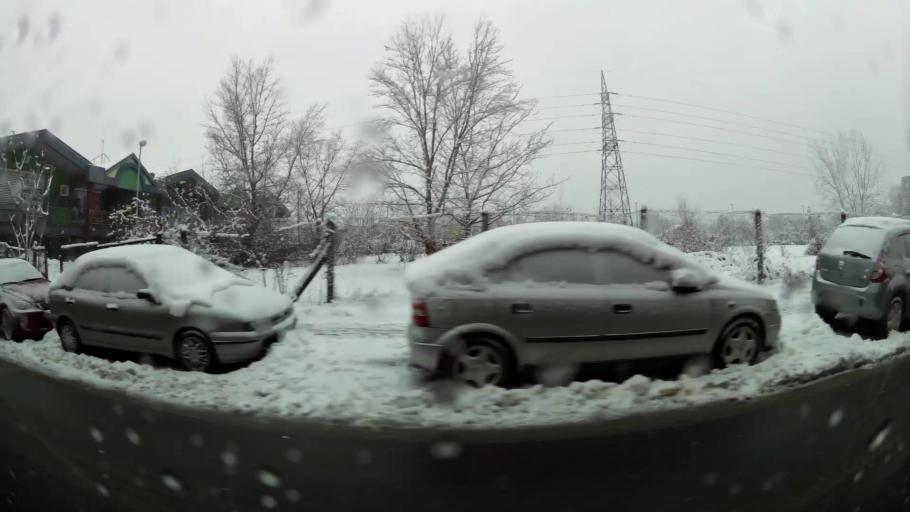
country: RS
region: Central Serbia
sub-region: Belgrade
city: Novi Beograd
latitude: 44.8029
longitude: 20.3952
